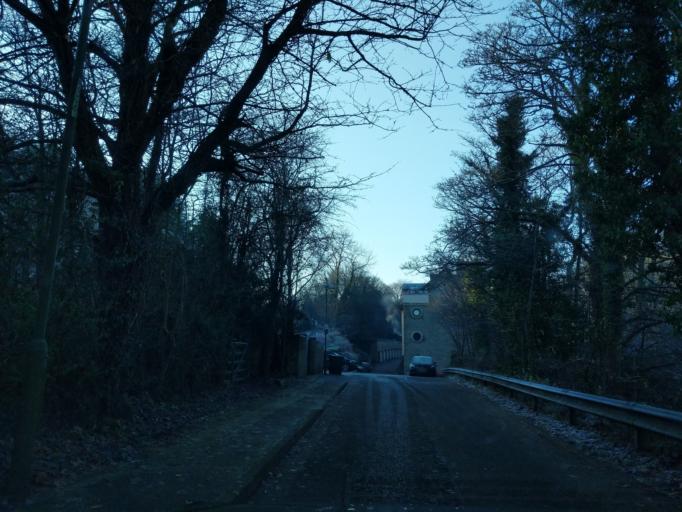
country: GB
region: Scotland
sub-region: Edinburgh
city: Colinton
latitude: 55.9059
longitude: -3.2716
